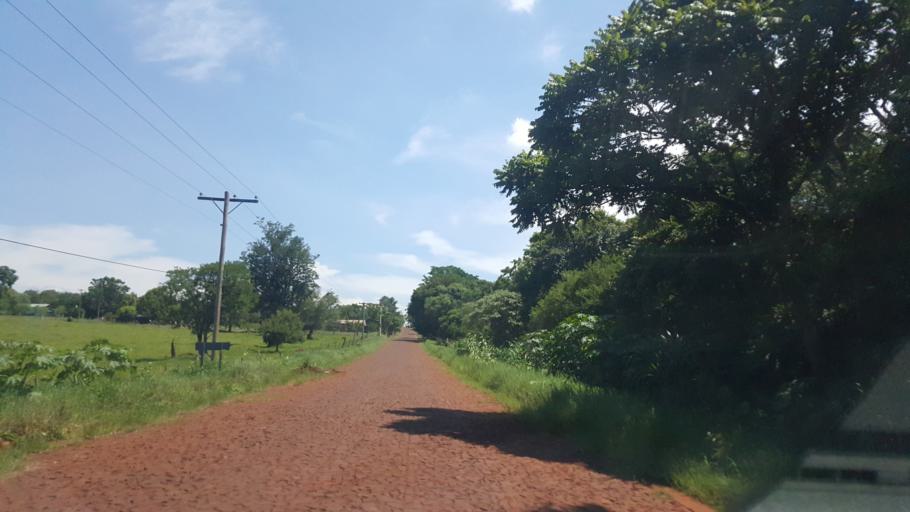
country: AR
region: Misiones
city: Capiovi
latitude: -26.9240
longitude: -55.0523
